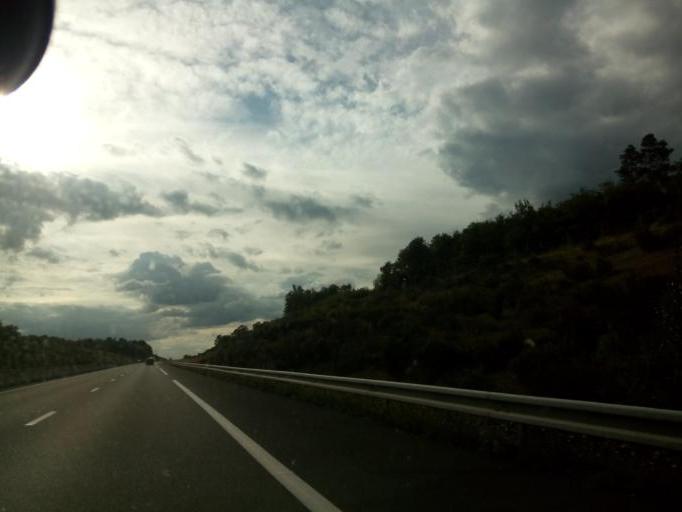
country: FR
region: Centre
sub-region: Departement du Loir-et-Cher
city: Thesee
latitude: 47.2926
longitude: 1.2788
